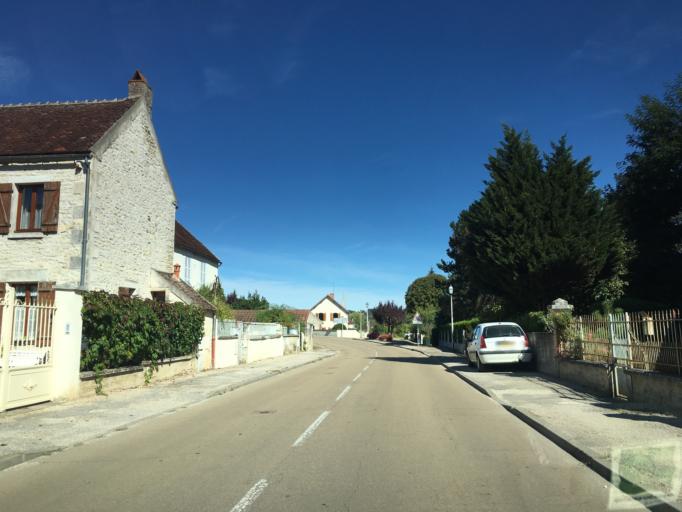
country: FR
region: Bourgogne
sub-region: Departement de l'Yonne
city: Vermenton
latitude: 47.6071
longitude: 3.6788
